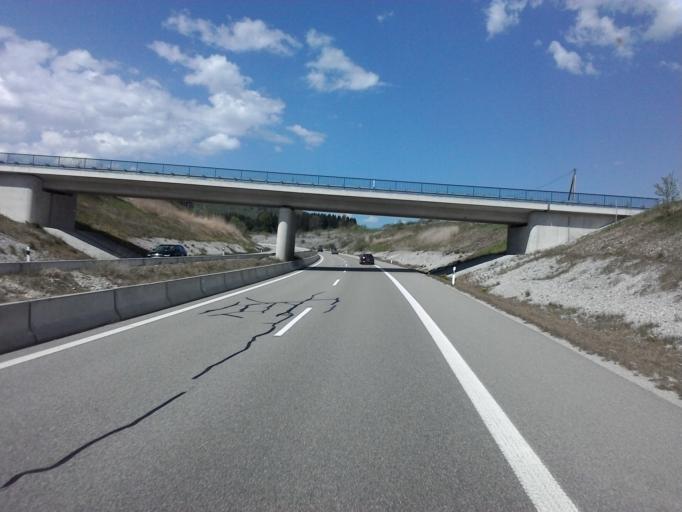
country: DE
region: Bavaria
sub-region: Swabia
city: Hopferau
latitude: 47.6164
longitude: 10.6614
